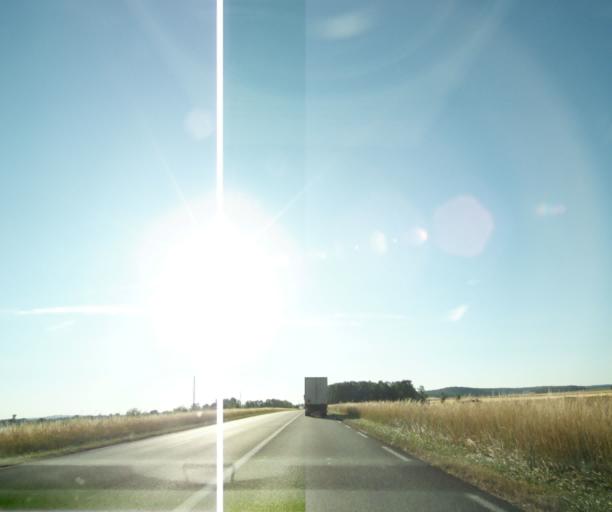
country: FR
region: Ile-de-France
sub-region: Departement de Seine-et-Marne
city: Varennes-sur-Seine
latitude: 48.3611
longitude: 2.9168
